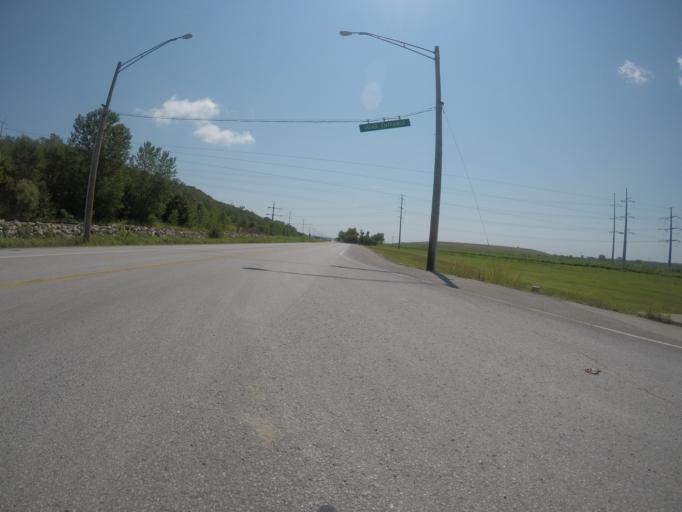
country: US
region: Missouri
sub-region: Platte County
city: Weston
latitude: 39.4585
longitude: -94.9678
